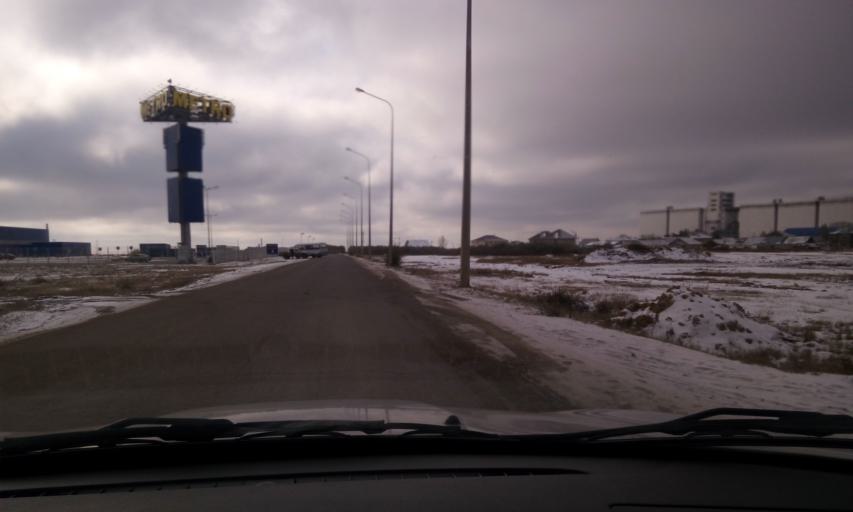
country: KZ
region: Astana Qalasy
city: Astana
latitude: 51.1333
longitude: 71.5442
